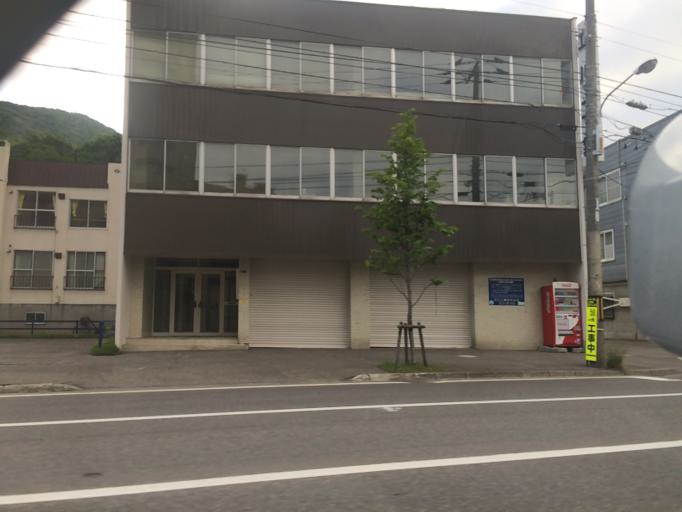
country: JP
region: Hokkaido
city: Sapporo
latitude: 43.0316
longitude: 141.3365
